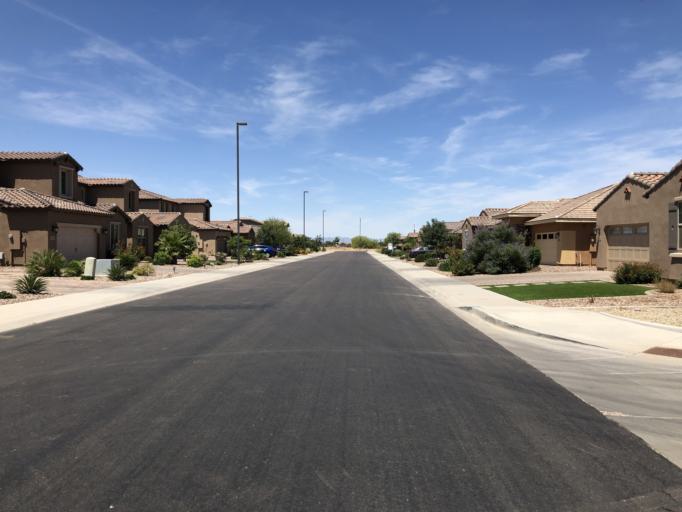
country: US
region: Arizona
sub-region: Maricopa County
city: Queen Creek
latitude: 33.2472
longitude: -111.7162
